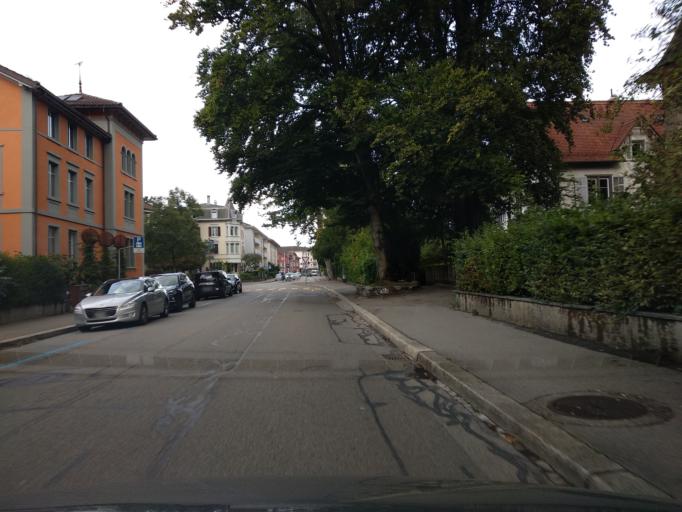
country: CH
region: Zurich
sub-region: Bezirk Winterthur
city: Winterthur
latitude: 47.5053
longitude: 8.7241
